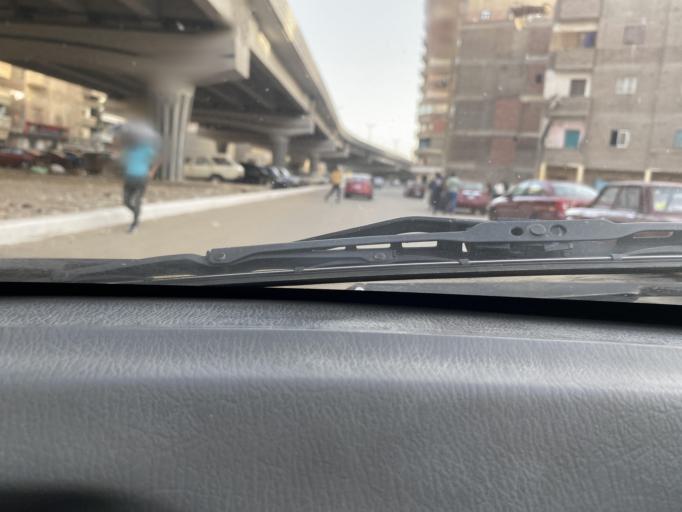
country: EG
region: Muhafazat al Qahirah
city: Cairo
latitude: 30.1203
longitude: 31.2970
